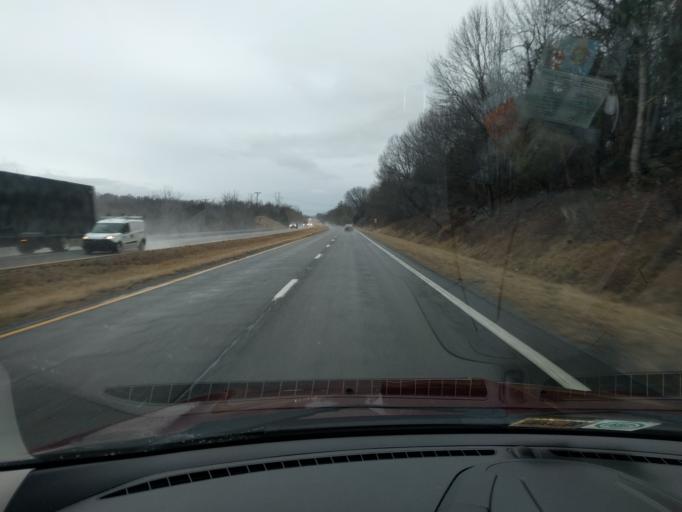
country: US
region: Virginia
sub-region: Giles County
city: Pembroke
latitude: 37.3038
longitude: -80.5710
